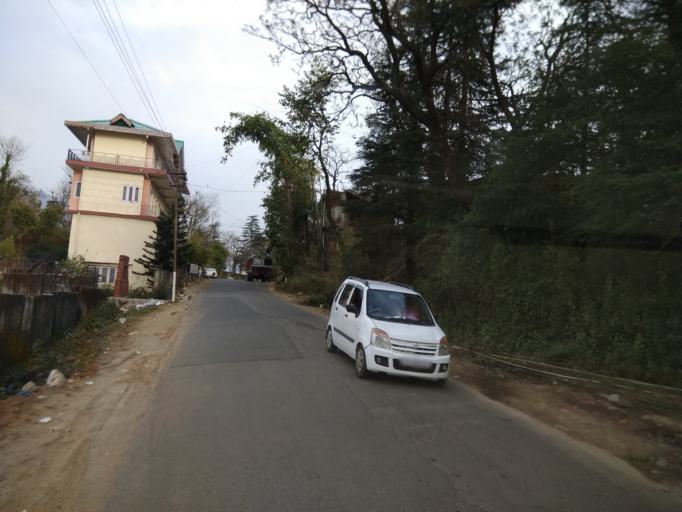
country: IN
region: Himachal Pradesh
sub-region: Kangra
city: Palampur
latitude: 32.1141
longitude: 76.5203
